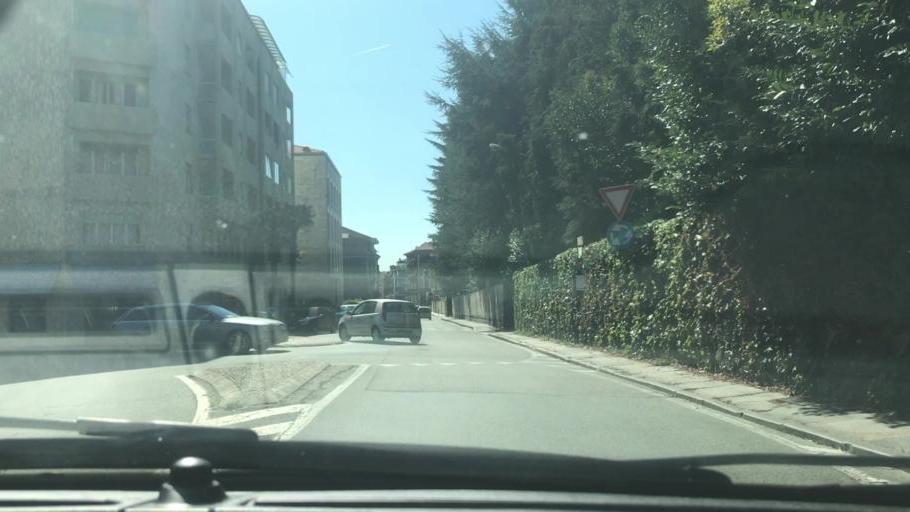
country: IT
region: Piedmont
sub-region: Provincia di Biella
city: Biella
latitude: 45.5718
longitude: 8.0505
